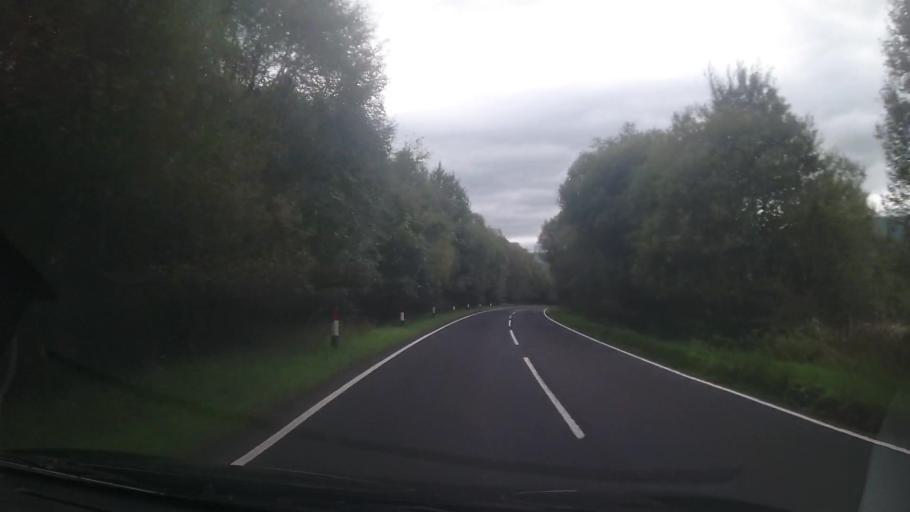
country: GB
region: Scotland
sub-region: Argyll and Bute
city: Garelochhead
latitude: 56.2260
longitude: -4.9863
